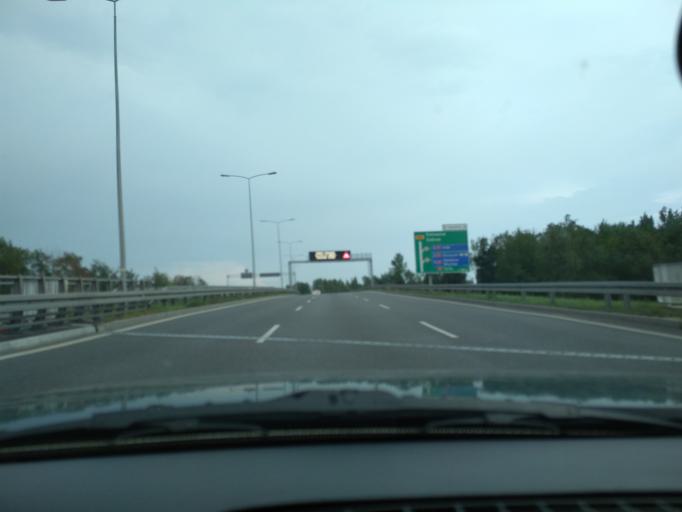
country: PL
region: Silesian Voivodeship
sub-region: Gliwice
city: Gliwice
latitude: 50.2830
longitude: 18.7124
